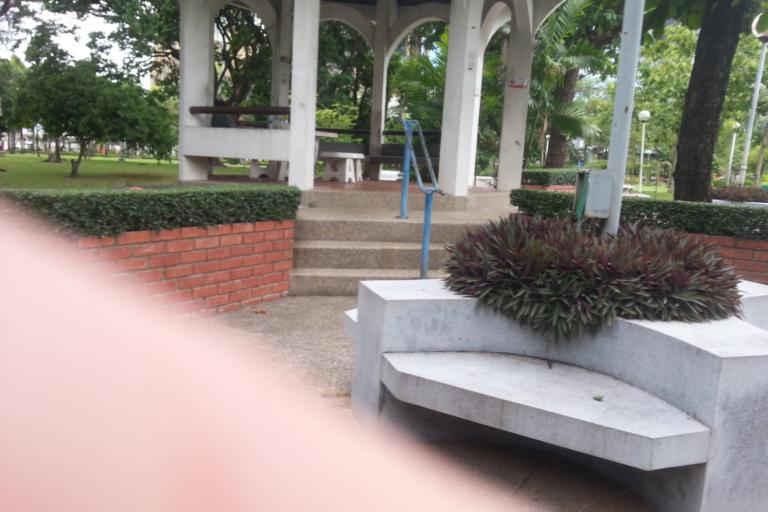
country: TH
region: Bangkok
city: Chatuchak
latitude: 13.8099
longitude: 100.5566
